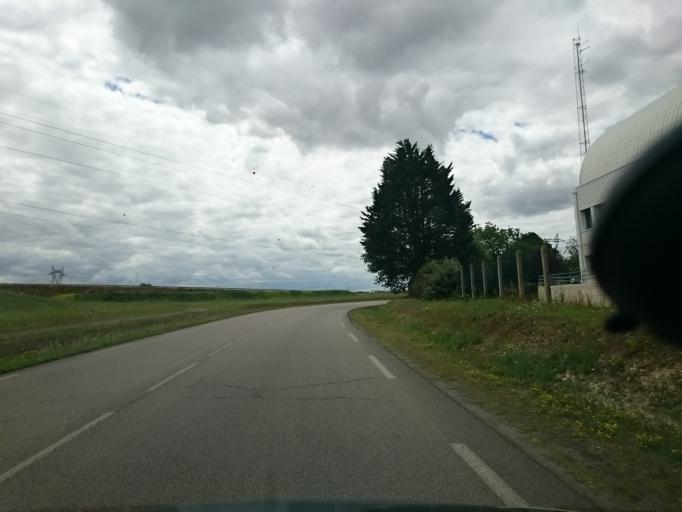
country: FR
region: Lower Normandy
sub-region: Departement du Calvados
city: Ifs
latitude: 49.1385
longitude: -0.3355
